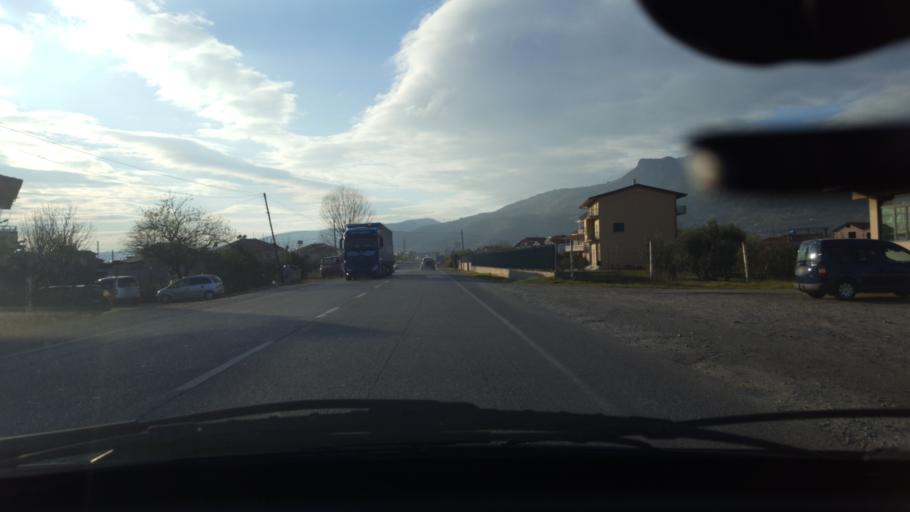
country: AL
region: Elbasan
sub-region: Rrethi i Elbasanit
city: Bradashesh
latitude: 41.0995
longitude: 20.0426
